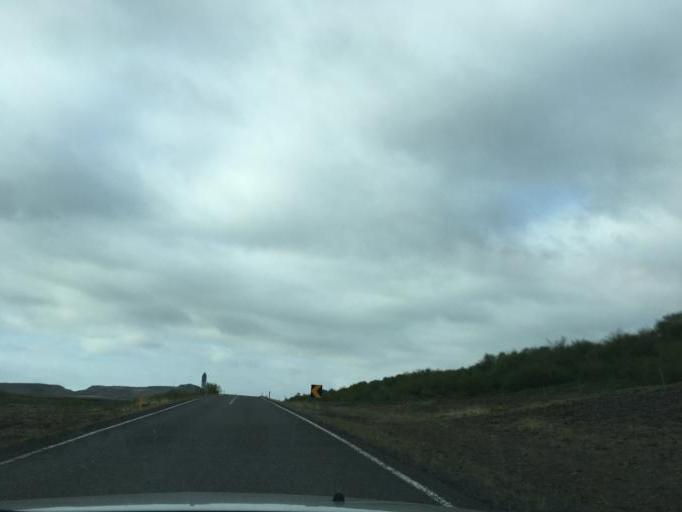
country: IS
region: South
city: Vestmannaeyjar
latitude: 64.2609
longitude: -20.2210
